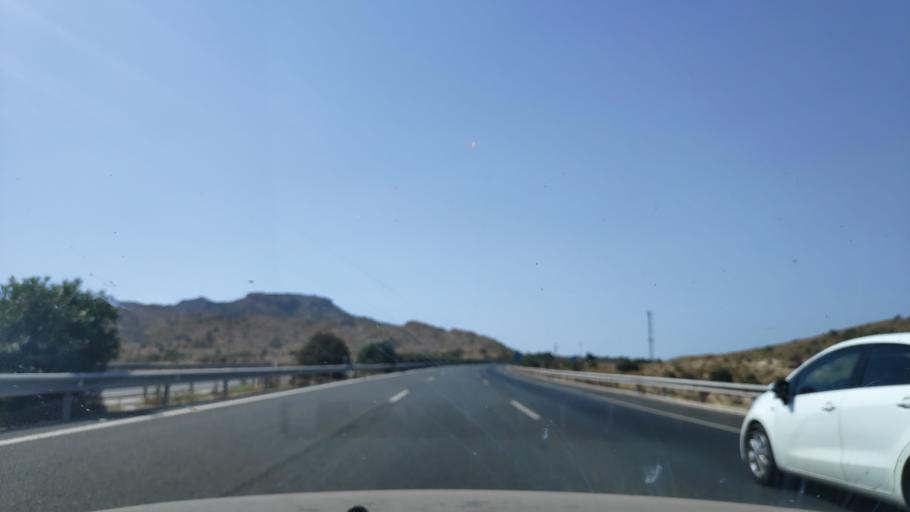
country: ES
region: Murcia
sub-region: Murcia
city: Ulea
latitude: 38.1656
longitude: -1.3052
